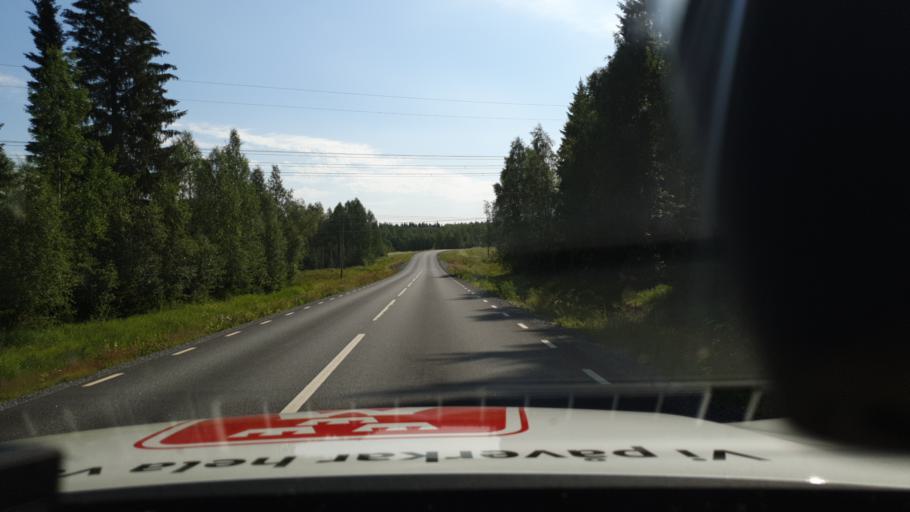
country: SE
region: Norrbotten
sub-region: Bodens Kommun
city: Saevast
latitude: 65.8444
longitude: 21.7849
